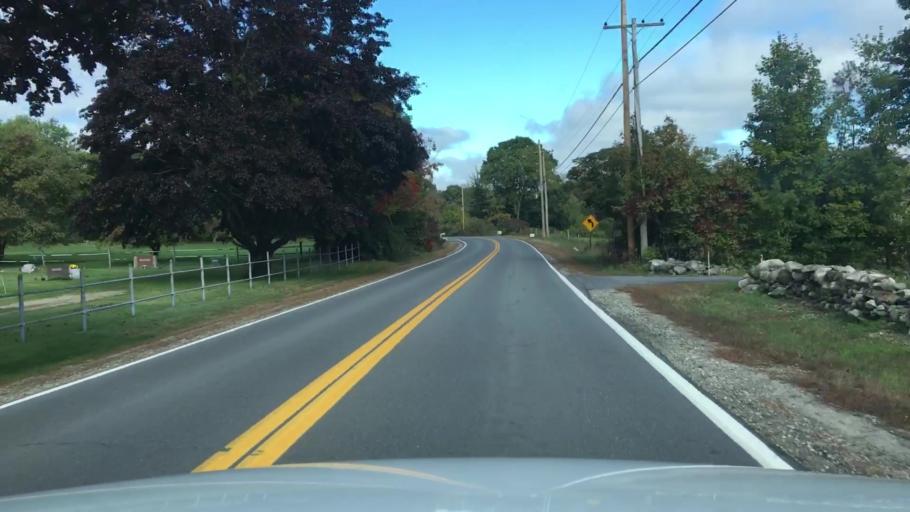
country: US
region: Maine
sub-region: Sagadahoc County
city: North Bath
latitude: 43.9860
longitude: -69.8900
